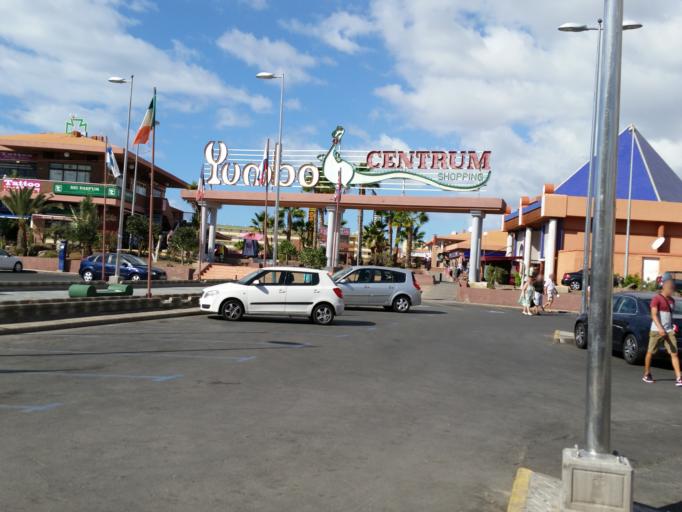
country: ES
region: Canary Islands
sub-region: Provincia de Las Palmas
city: Playa del Ingles
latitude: 27.7585
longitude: -15.5751
